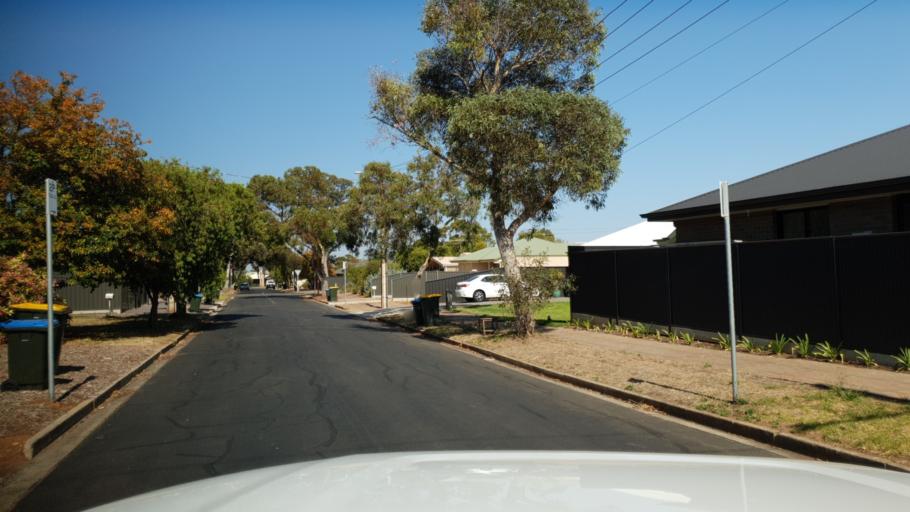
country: AU
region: South Australia
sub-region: Mitcham
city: Clapham
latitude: -34.9941
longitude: 138.5876
